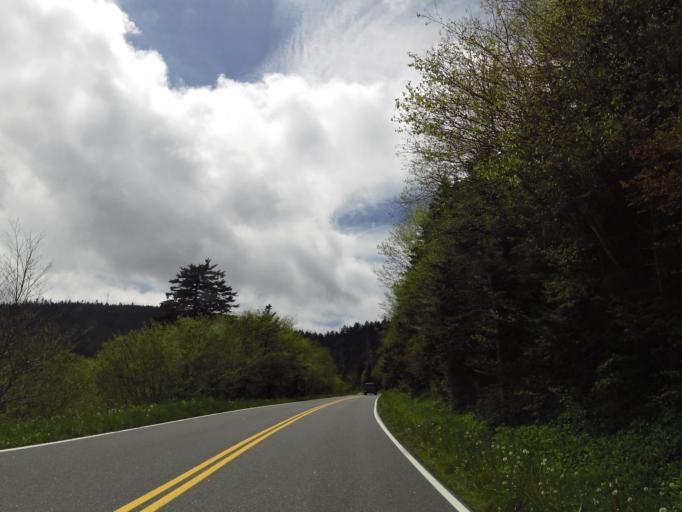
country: US
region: North Carolina
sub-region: Swain County
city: Bryson City
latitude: 35.5652
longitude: -83.4883
